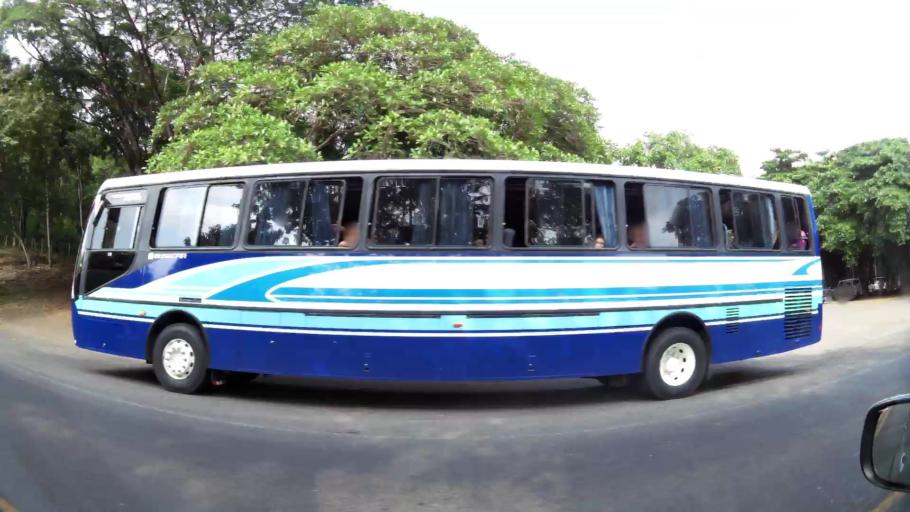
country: CR
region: Guanacaste
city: Juntas
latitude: 10.1789
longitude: -84.9326
